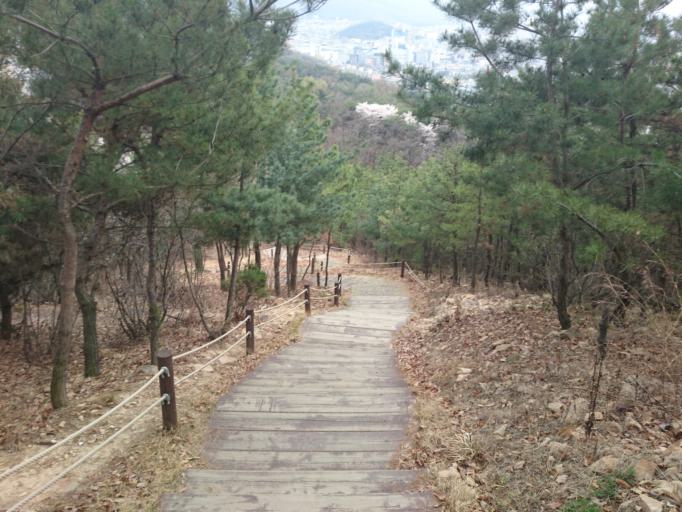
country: KR
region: Daegu
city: Daegu
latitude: 35.8465
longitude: 128.5563
